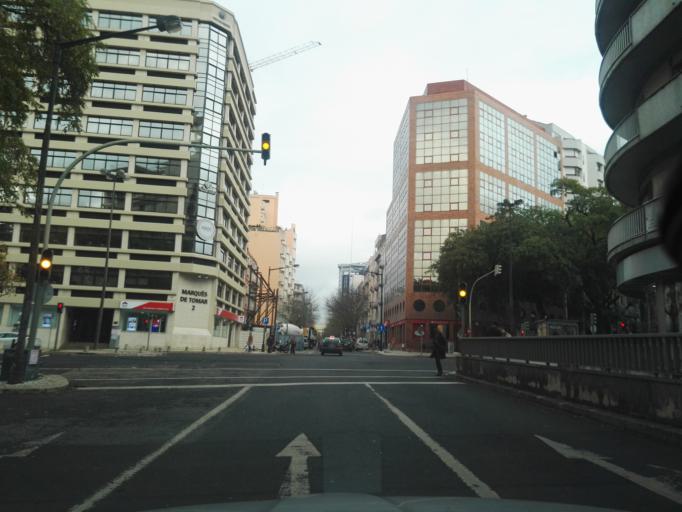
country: PT
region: Lisbon
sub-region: Lisbon
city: Lisbon
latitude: 38.7358
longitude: -9.1497
